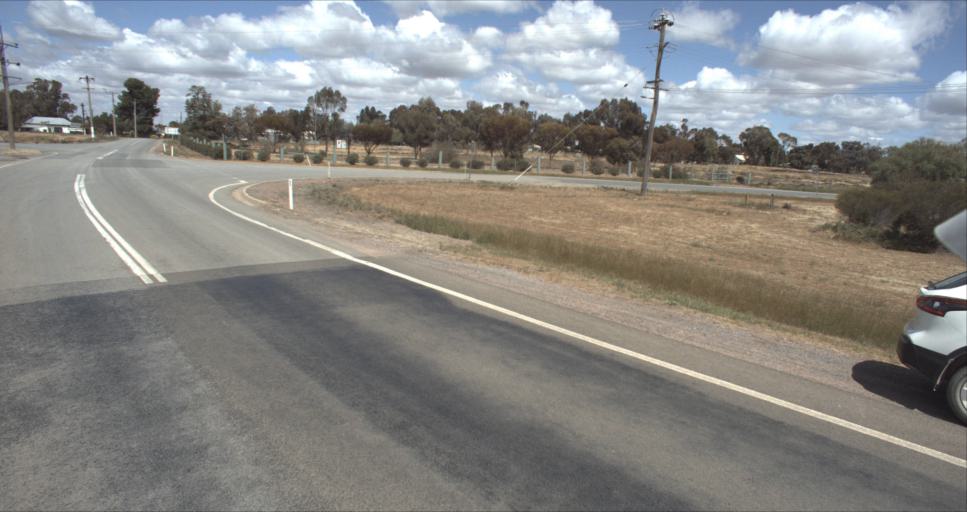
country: AU
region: New South Wales
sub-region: Murrumbidgee Shire
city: Darlington Point
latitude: -34.5162
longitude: 146.1855
